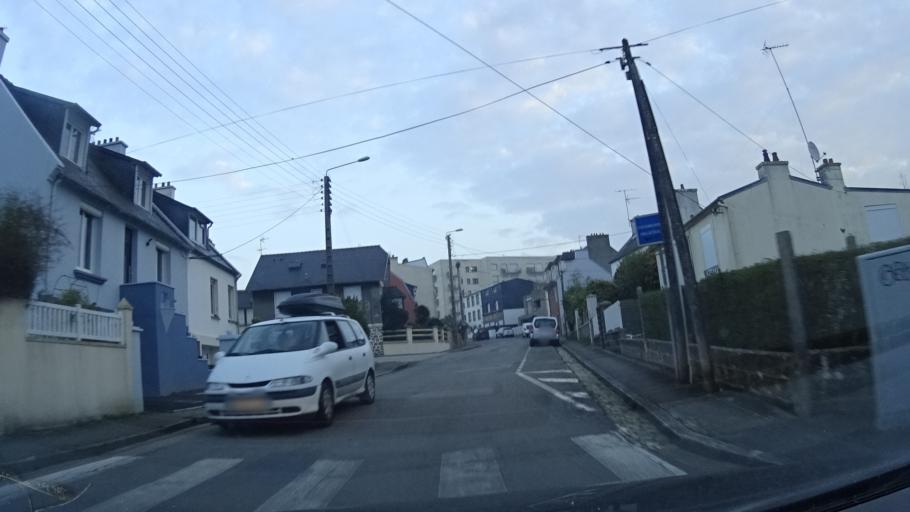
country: FR
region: Brittany
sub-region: Departement du Finistere
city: Brest
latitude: 48.3969
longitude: -4.4584
